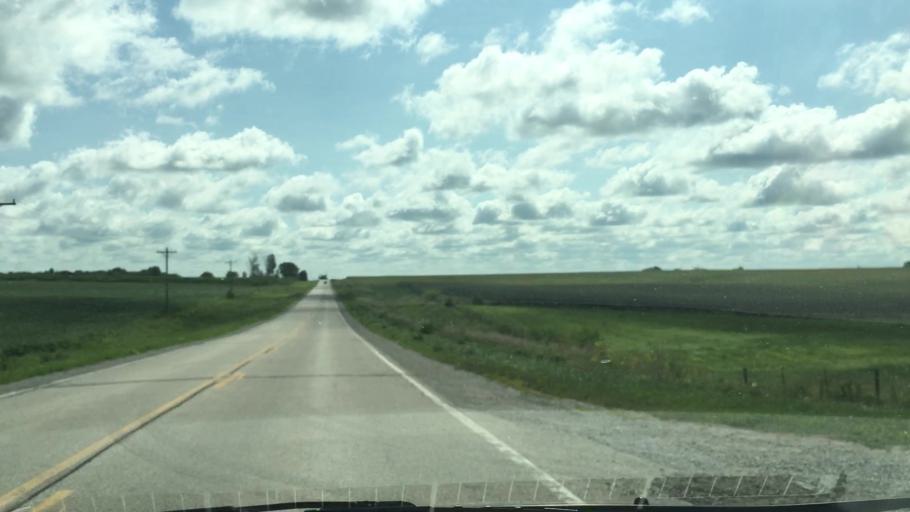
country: US
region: Iowa
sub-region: Johnson County
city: Solon
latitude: 41.8310
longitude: -91.4533
